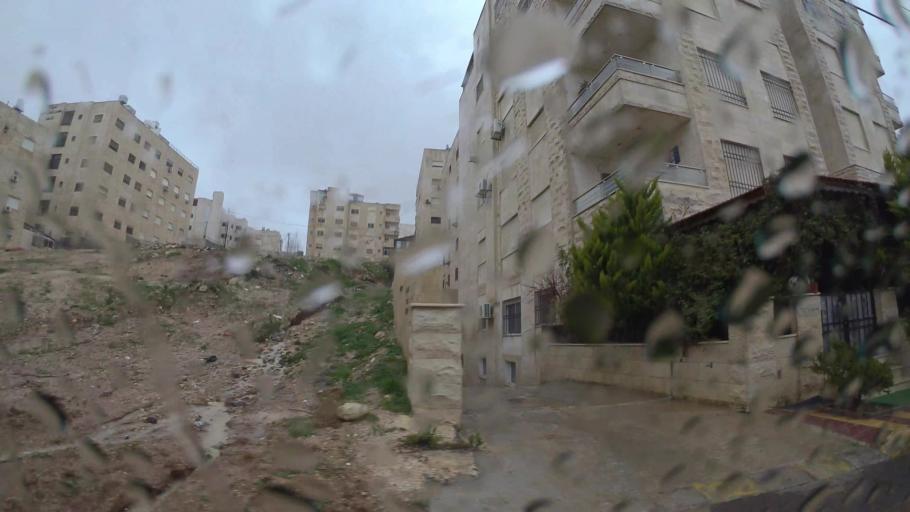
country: JO
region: Amman
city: Al Jubayhah
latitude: 32.0266
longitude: 35.8914
